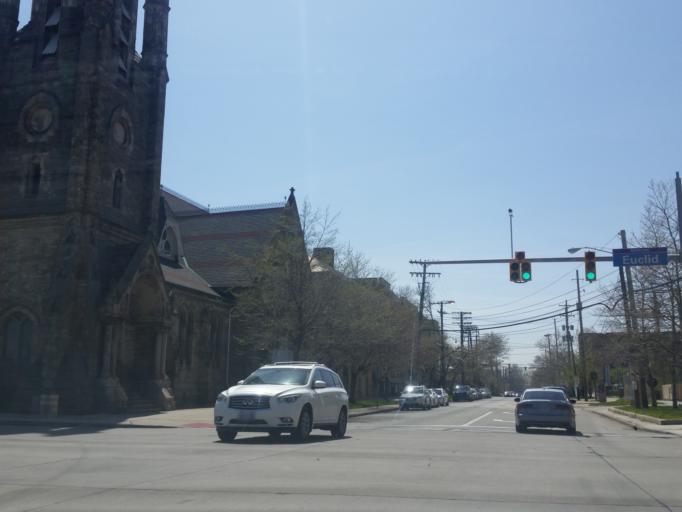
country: US
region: Ohio
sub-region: Cuyahoga County
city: Cleveland
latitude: 41.5037
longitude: -81.6581
